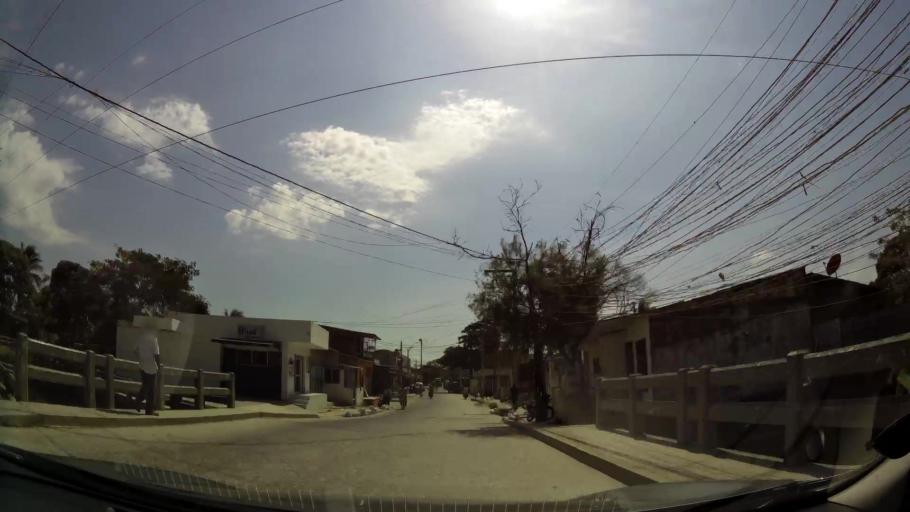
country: CO
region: Atlantico
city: Barranquilla
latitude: 10.9677
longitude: -74.8369
